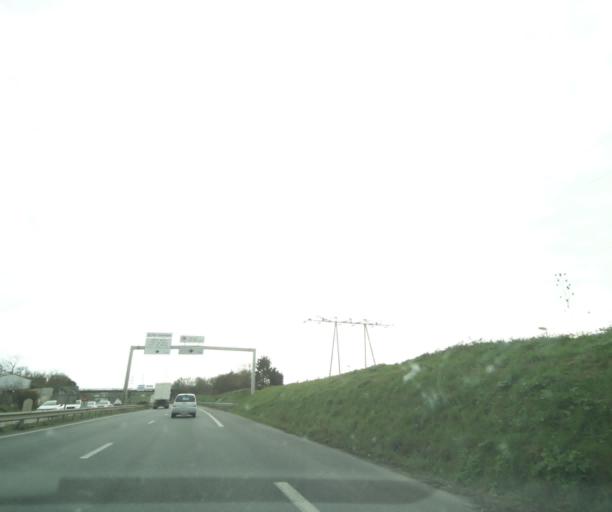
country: FR
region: Poitou-Charentes
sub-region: Departement de la Charente-Maritime
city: La Rochelle
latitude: 46.1684
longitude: -1.1914
